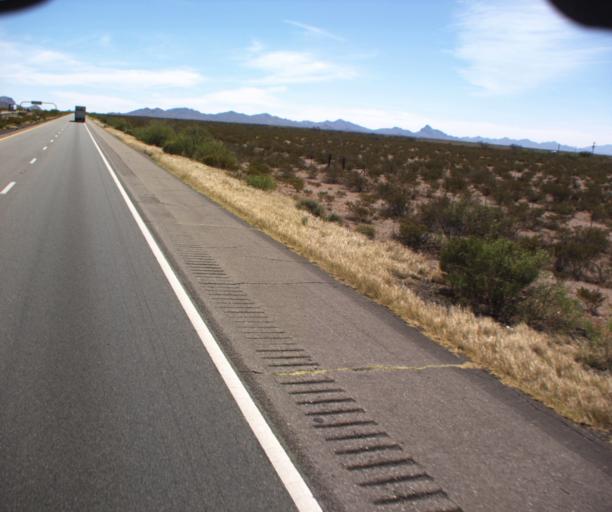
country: US
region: New Mexico
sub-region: Hidalgo County
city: Lordsburg
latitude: 32.2514
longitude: -109.1533
